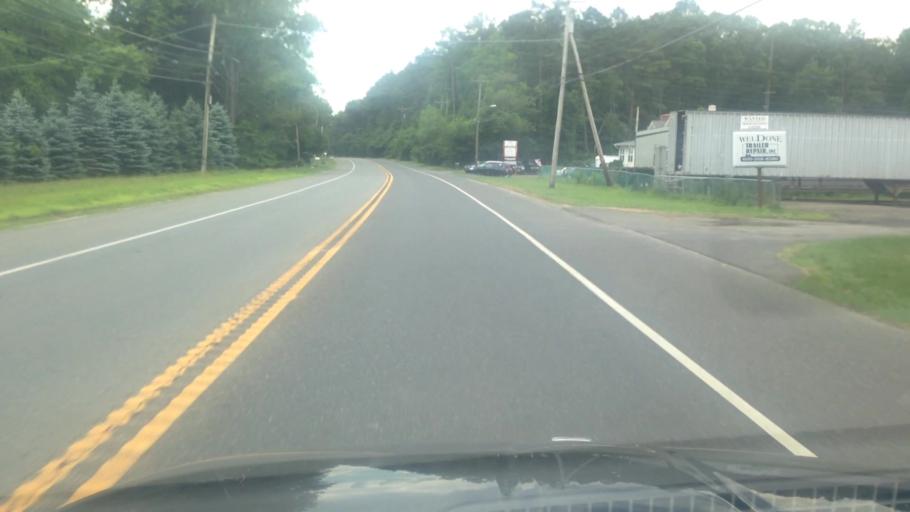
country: US
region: New Jersey
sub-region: Burlington County
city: Leisuretowne
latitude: 39.8394
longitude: -74.7359
